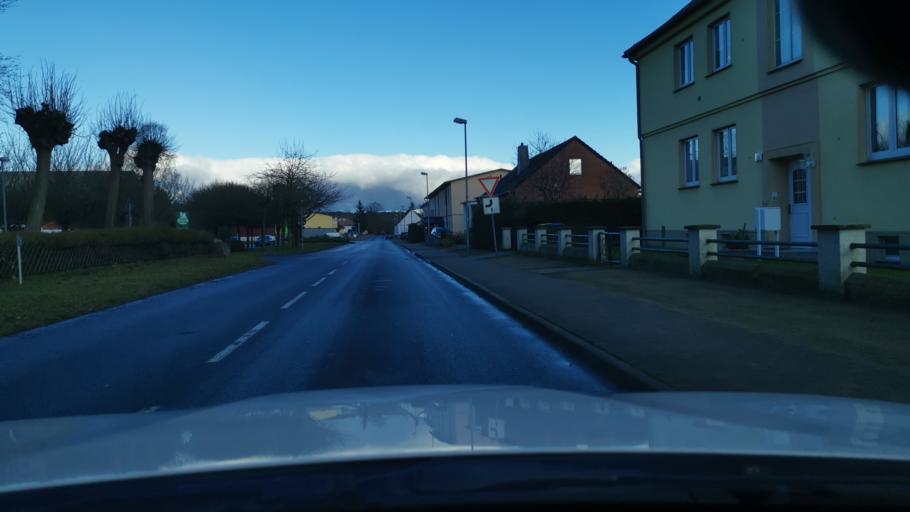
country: DE
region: Mecklenburg-Vorpommern
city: Tessin
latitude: 54.0296
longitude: 12.4694
